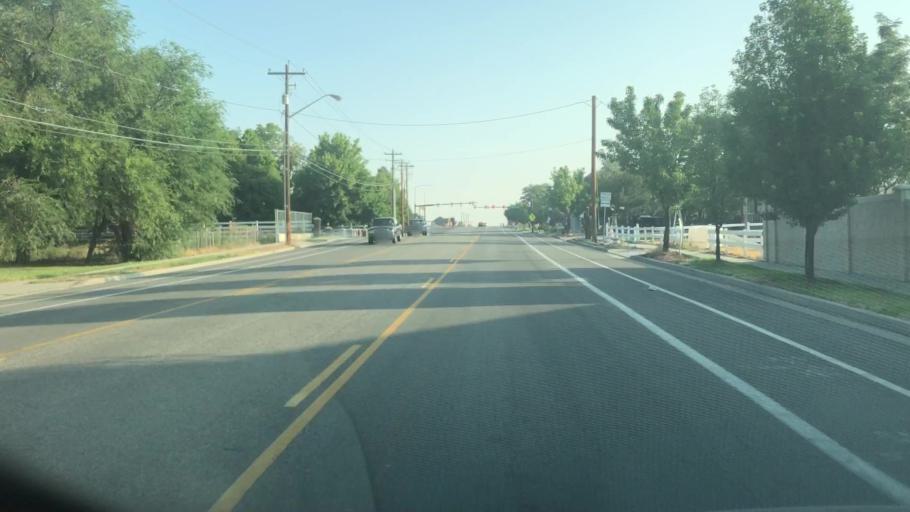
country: US
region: Utah
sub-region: Salt Lake County
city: South Jordan
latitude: 40.5598
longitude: -111.9291
